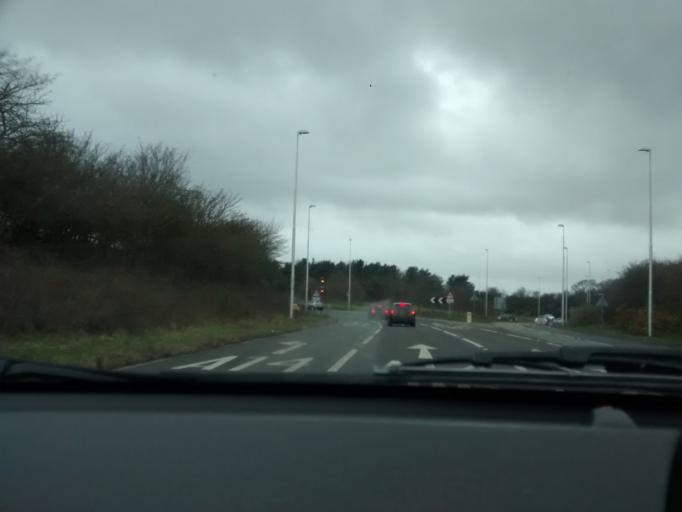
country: GB
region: England
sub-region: Suffolk
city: Felixstowe
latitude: 51.9780
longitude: 1.3344
